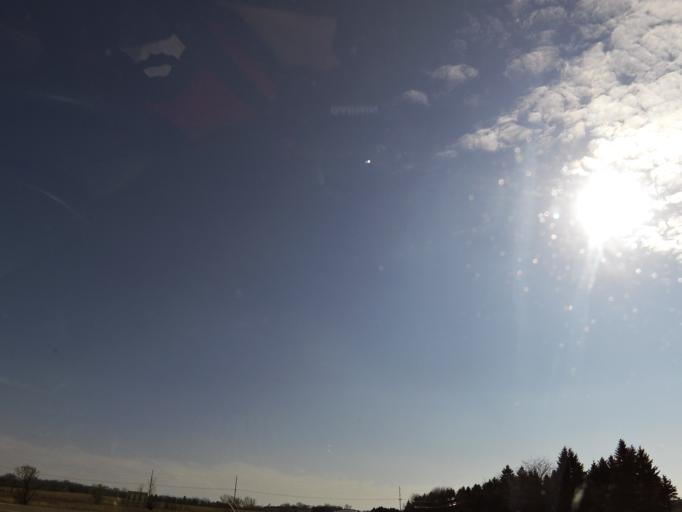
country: US
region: Minnesota
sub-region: Steele County
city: Owatonna
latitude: 44.0797
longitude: -93.2490
